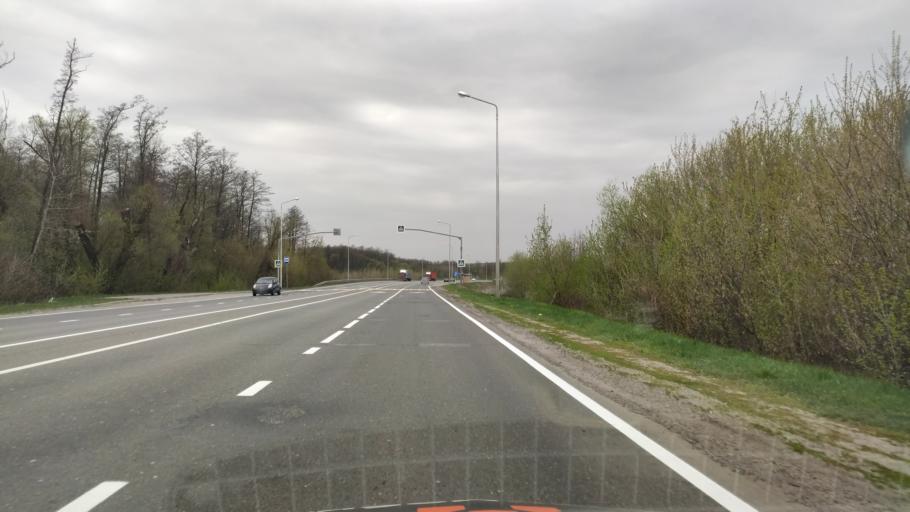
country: RU
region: Belgorod
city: Staryy Oskol
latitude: 51.3498
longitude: 37.8267
